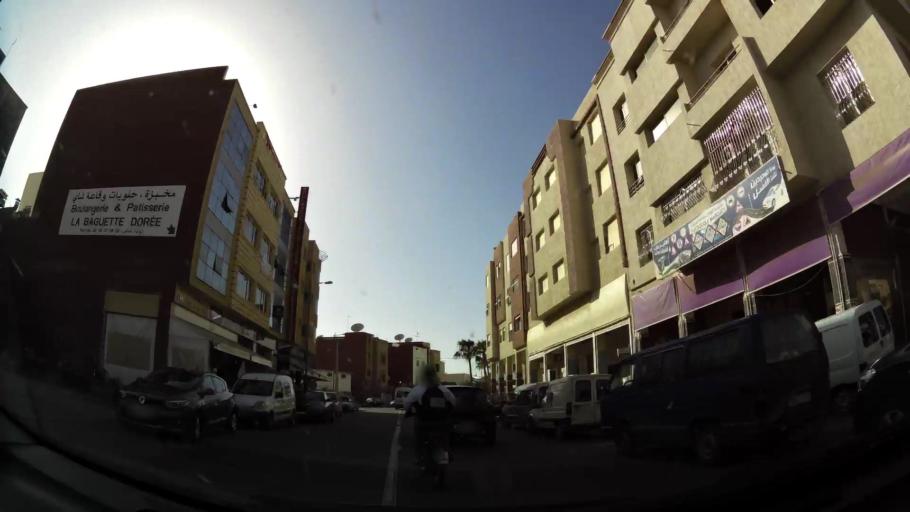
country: MA
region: Souss-Massa-Draa
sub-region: Inezgane-Ait Mellou
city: Inezgane
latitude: 30.3631
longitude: -9.5259
